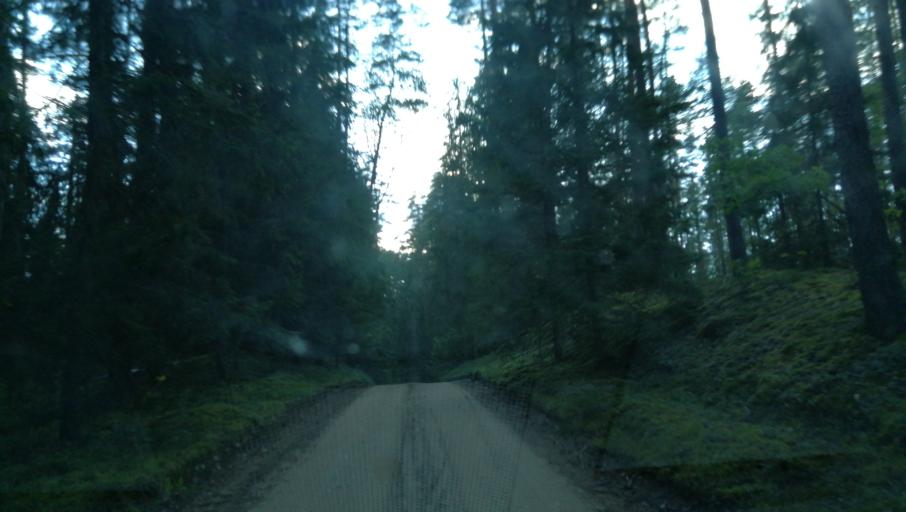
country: LV
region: Cesu Rajons
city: Cesis
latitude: 57.2902
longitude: 25.1931
